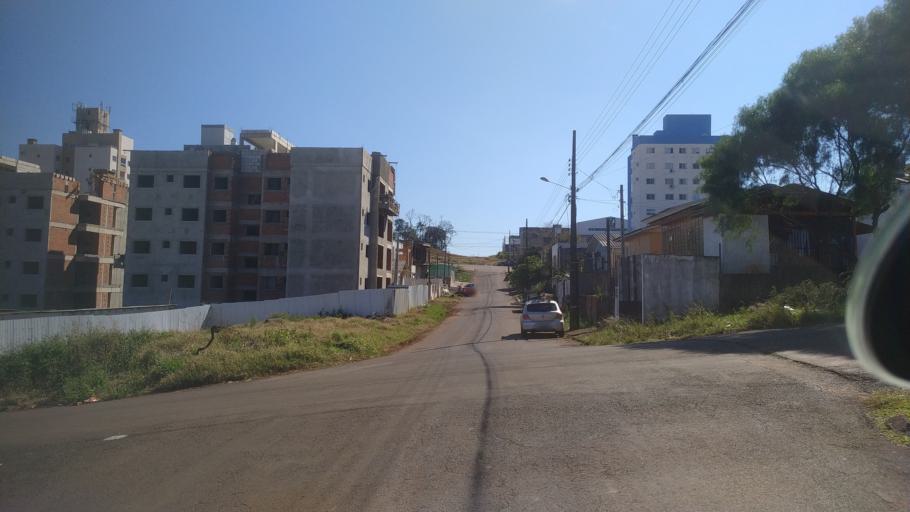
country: BR
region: Santa Catarina
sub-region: Chapeco
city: Chapeco
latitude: -27.0908
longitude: -52.5902
